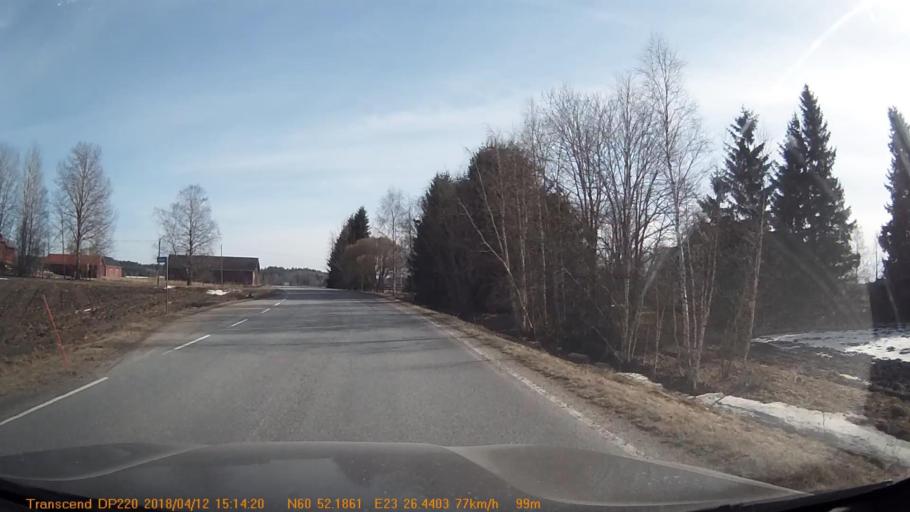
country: FI
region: Haeme
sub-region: Forssa
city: Jokioinen
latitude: 60.8696
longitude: 23.4408
